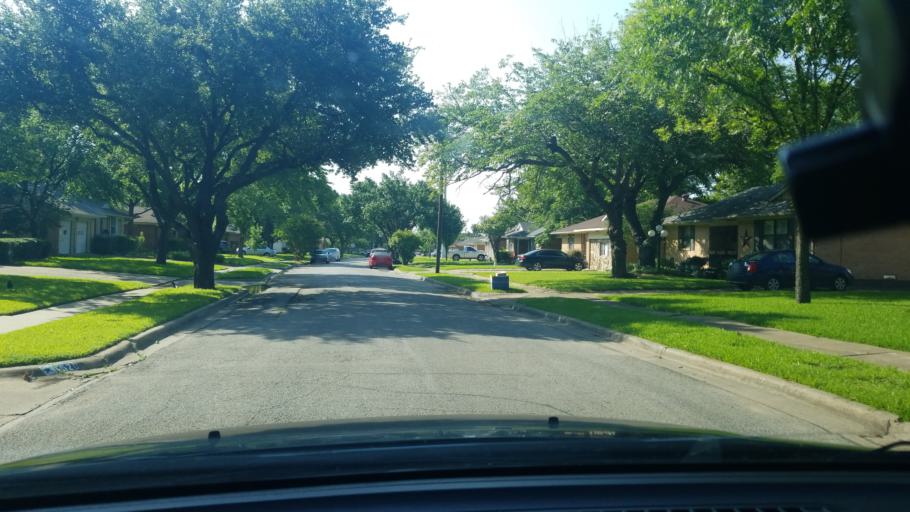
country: US
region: Texas
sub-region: Dallas County
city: Mesquite
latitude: 32.8250
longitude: -96.6433
